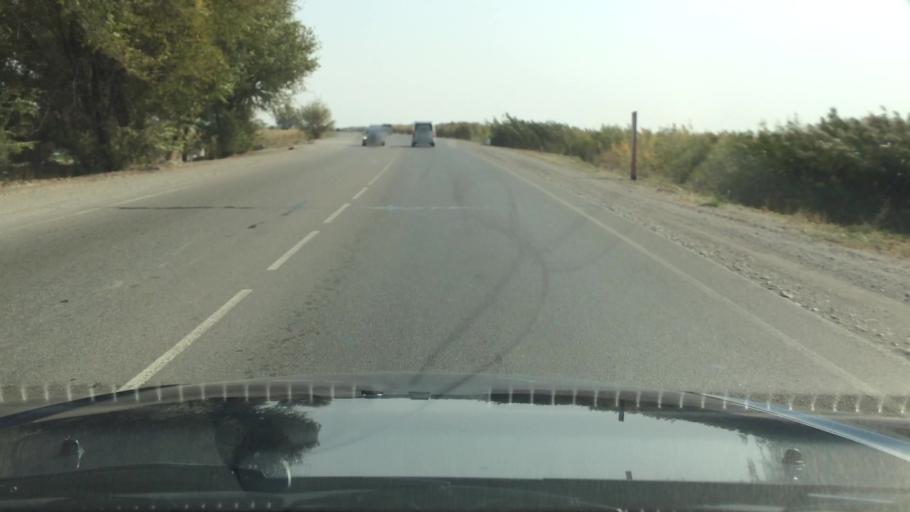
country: KG
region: Chuy
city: Lebedinovka
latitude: 42.9204
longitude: 74.7118
